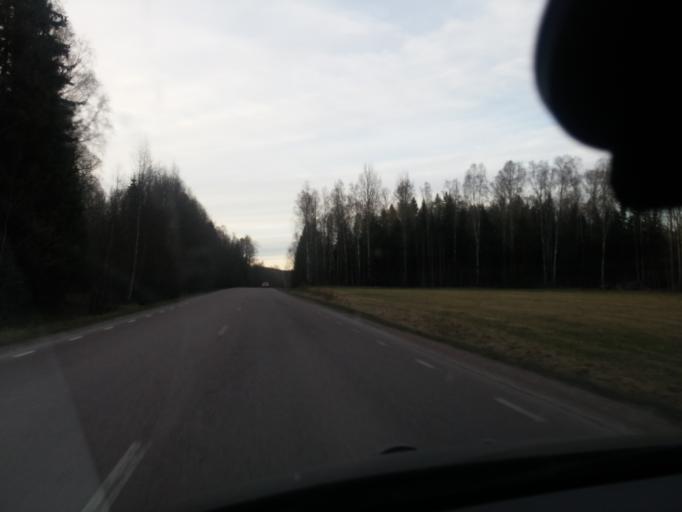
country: SE
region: Dalarna
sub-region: Borlange Kommun
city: Borlaenge
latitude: 60.5285
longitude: 15.4124
